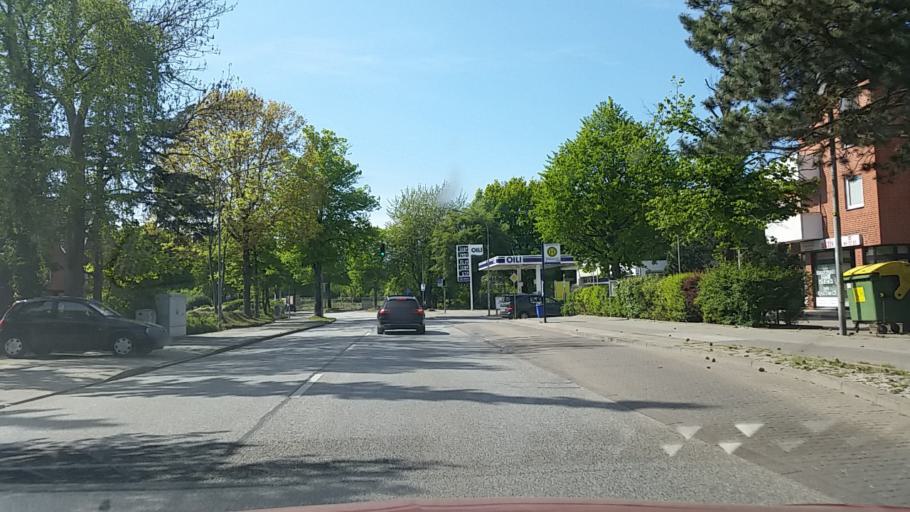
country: DE
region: Schleswig-Holstein
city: Stockelsdorf
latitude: 53.8499
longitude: 10.6486
